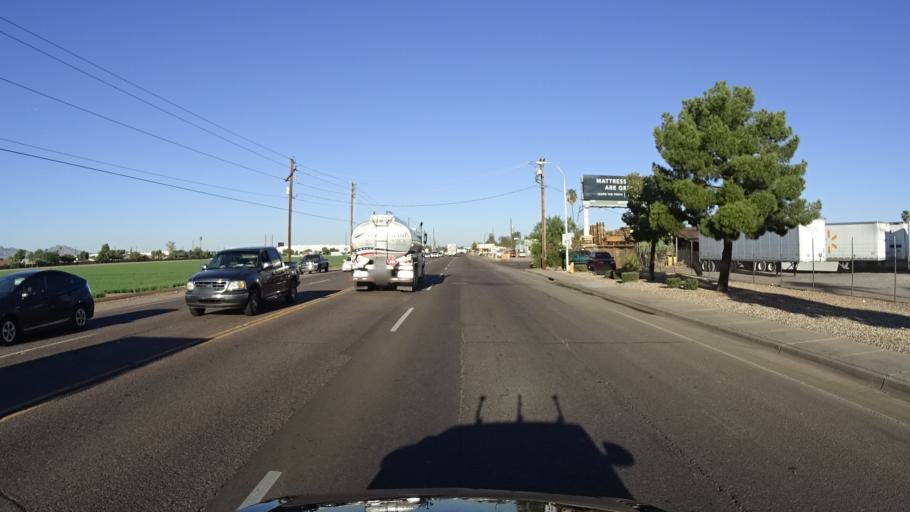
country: US
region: Arizona
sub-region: Maricopa County
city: Tolleson
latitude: 33.4372
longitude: -112.1988
